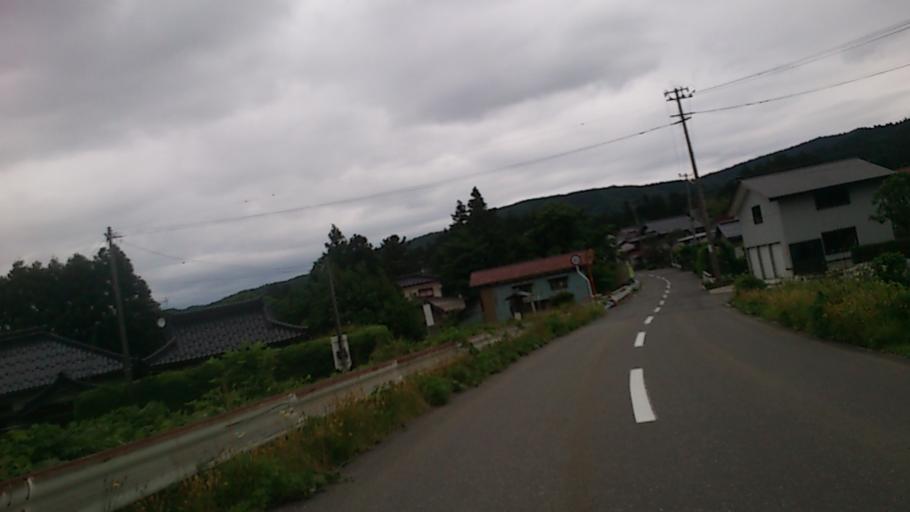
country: JP
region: Yamagata
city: Tsuruoka
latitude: 38.7390
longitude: 139.9605
